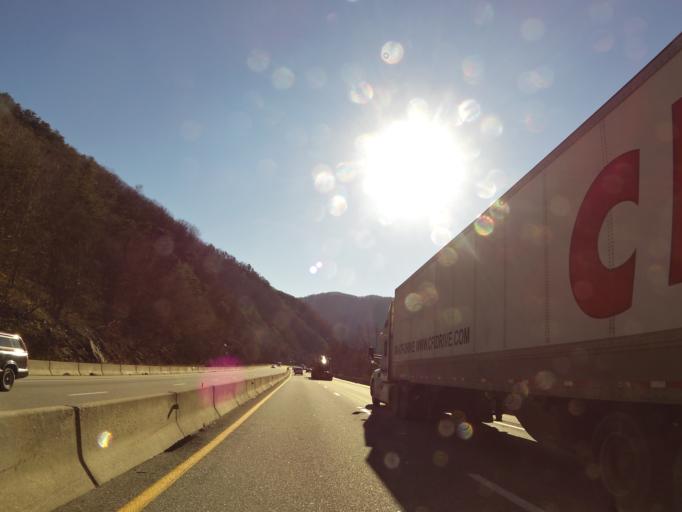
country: US
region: North Carolina
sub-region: Haywood County
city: Cove Creek
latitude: 35.7628
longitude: -83.0761
